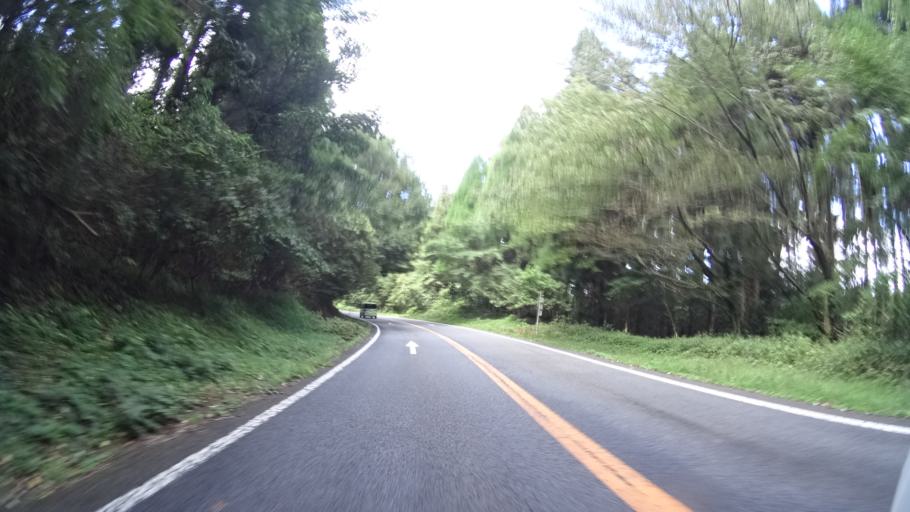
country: JP
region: Oita
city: Tsukawaki
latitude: 33.1967
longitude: 131.2541
